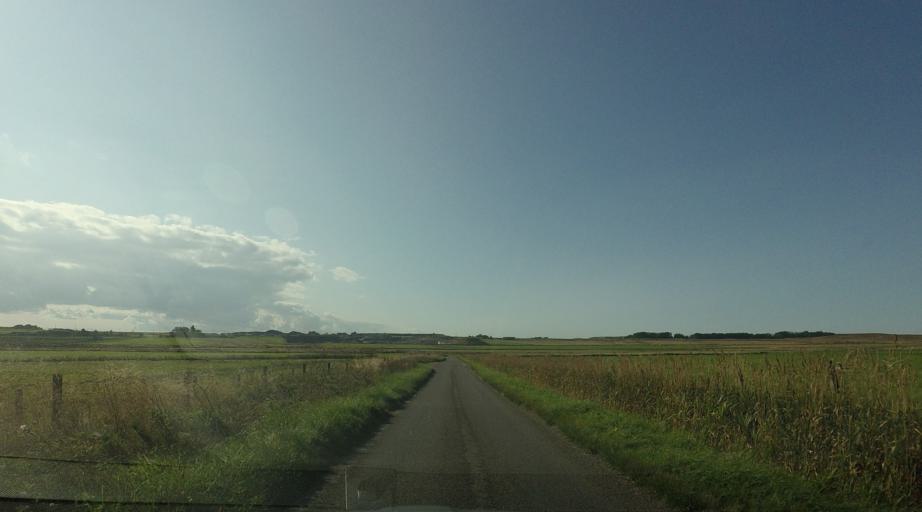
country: GB
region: Scotland
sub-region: Highland
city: Thurso
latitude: 58.4701
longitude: -3.4002
